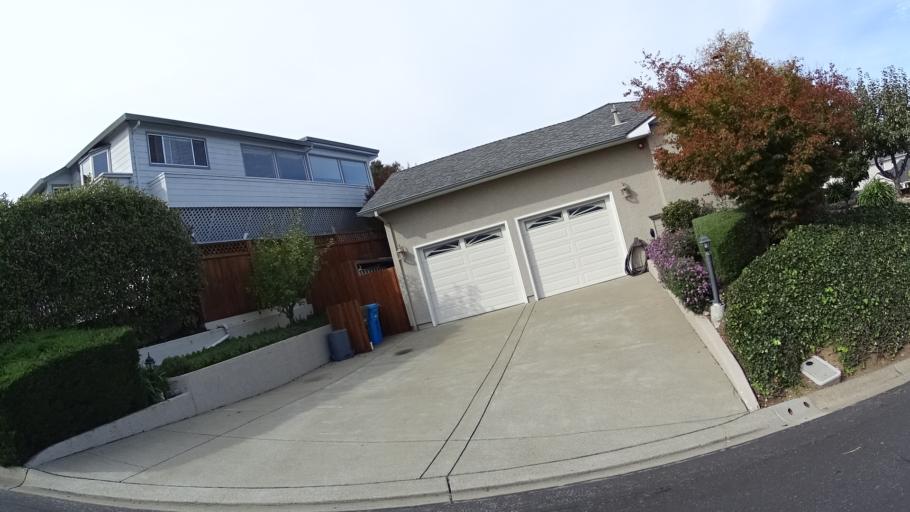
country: US
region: California
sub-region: San Mateo County
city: Hillsborough
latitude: 37.5750
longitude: -122.3941
